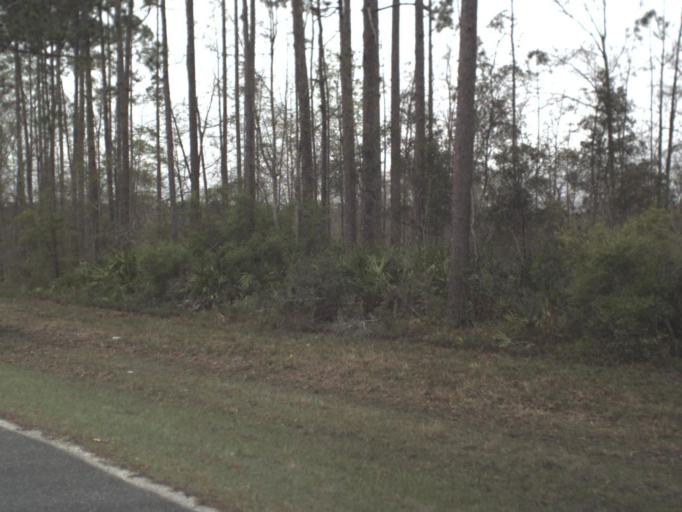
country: US
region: Florida
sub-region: Gulf County
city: Wewahitchka
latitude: 30.0106
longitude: -84.9787
